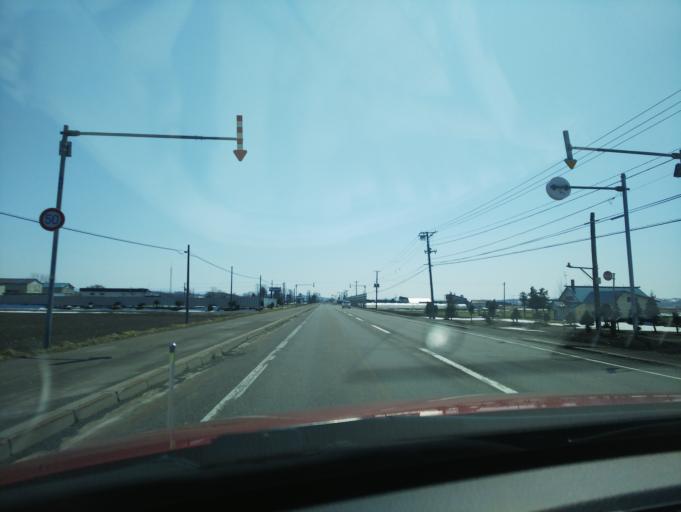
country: JP
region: Hokkaido
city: Nayoro
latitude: 44.2087
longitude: 142.3949
